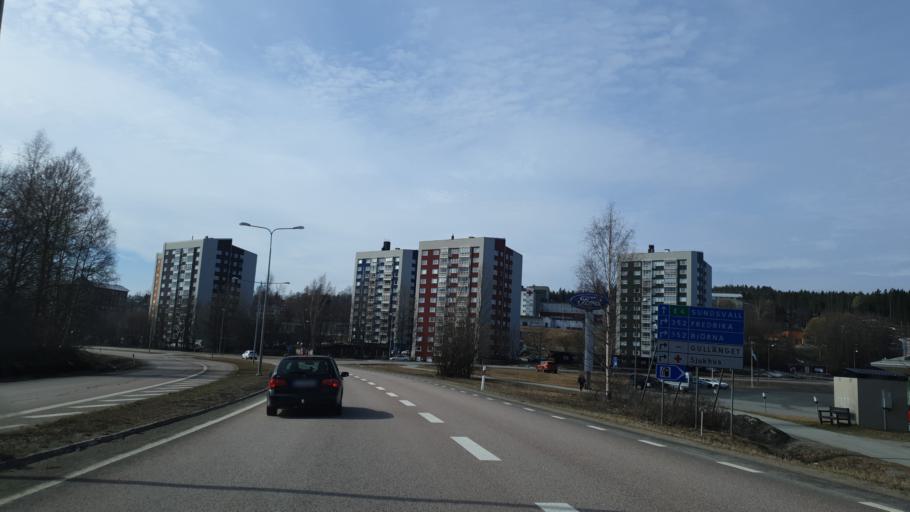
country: SE
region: Vaesternorrland
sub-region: OErnskoeldsviks Kommun
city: Ornskoldsvik
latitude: 63.3015
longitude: 18.7210
